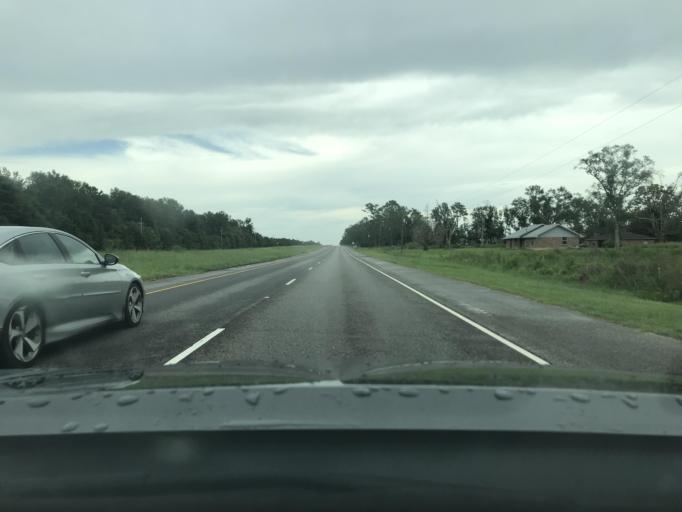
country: US
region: Louisiana
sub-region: Calcasieu Parish
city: Moss Bluff
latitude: 30.3944
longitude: -93.2275
